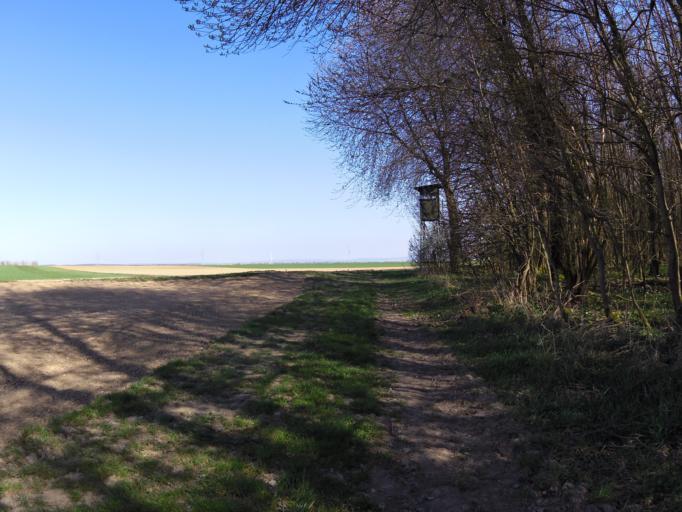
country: DE
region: Bavaria
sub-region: Regierungsbezirk Unterfranken
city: Kurnach
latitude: 49.8344
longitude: 10.0703
